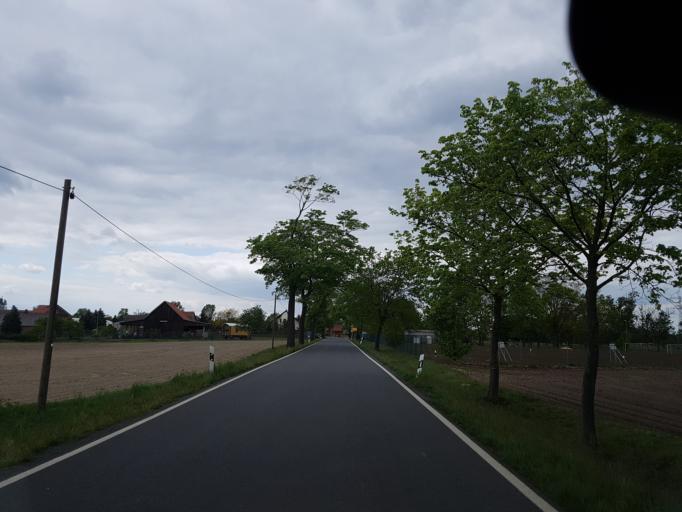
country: DE
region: Brandenburg
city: Bronkow
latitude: 51.6309
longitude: 13.9348
